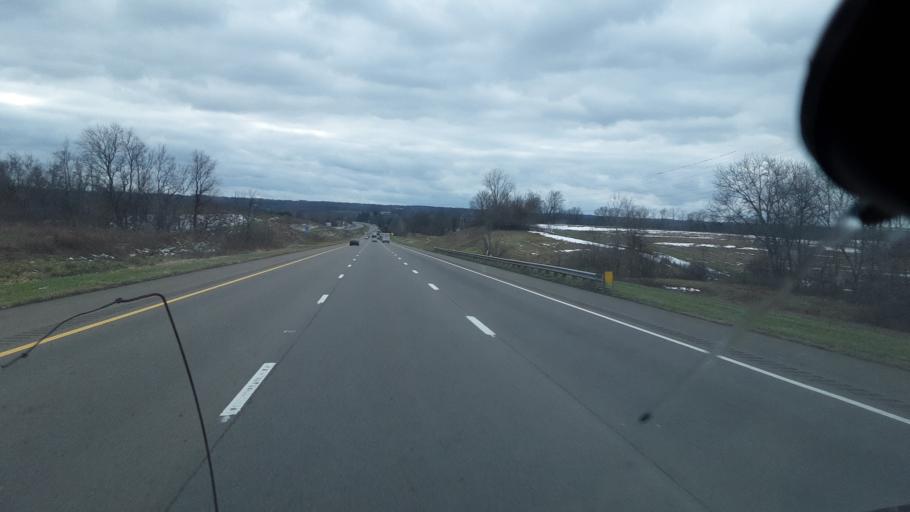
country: US
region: Ohio
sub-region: Ashland County
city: Ashland
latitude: 40.8060
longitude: -82.3793
